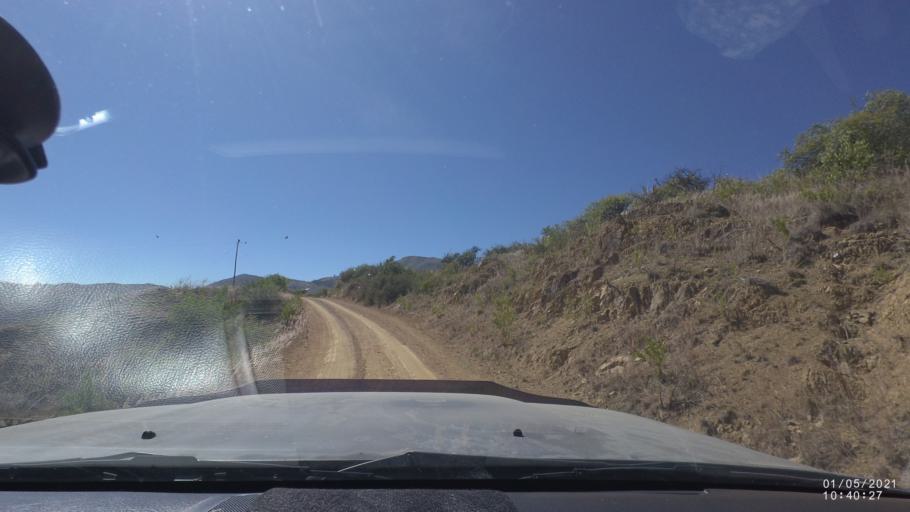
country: BO
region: Cochabamba
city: Capinota
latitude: -17.6059
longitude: -66.1817
